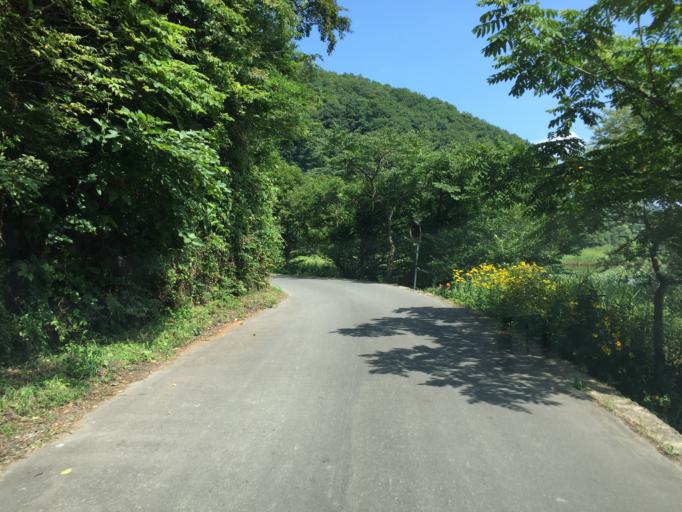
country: JP
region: Fukushima
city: Inawashiro
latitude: 37.4141
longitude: 140.0961
